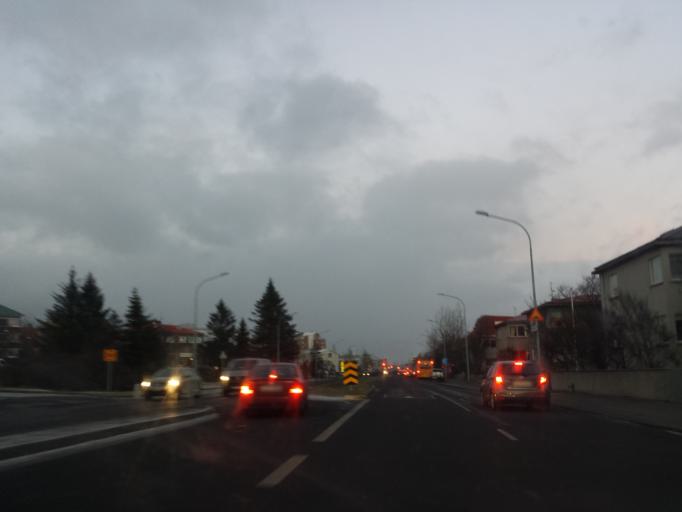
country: IS
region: Capital Region
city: Kopavogur
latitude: 64.1376
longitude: -21.9224
